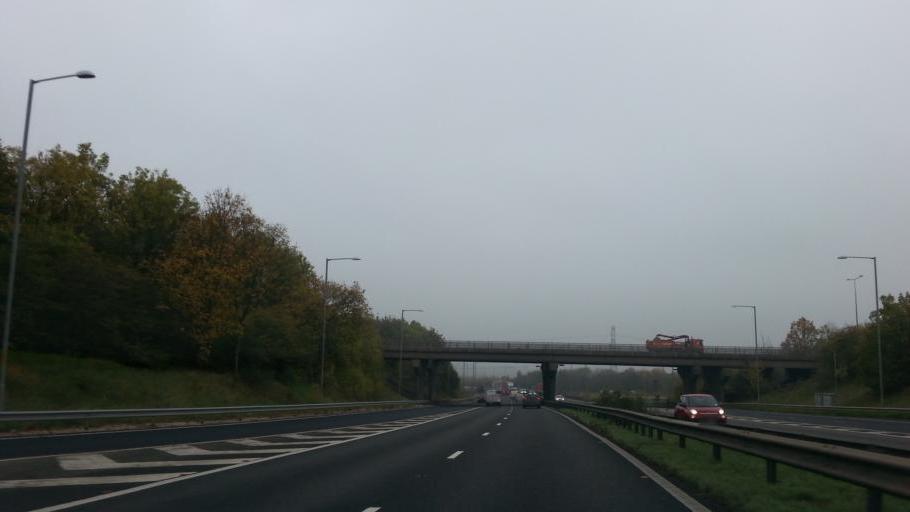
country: GB
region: England
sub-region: Doncaster
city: Marr
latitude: 53.5770
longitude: -1.2134
